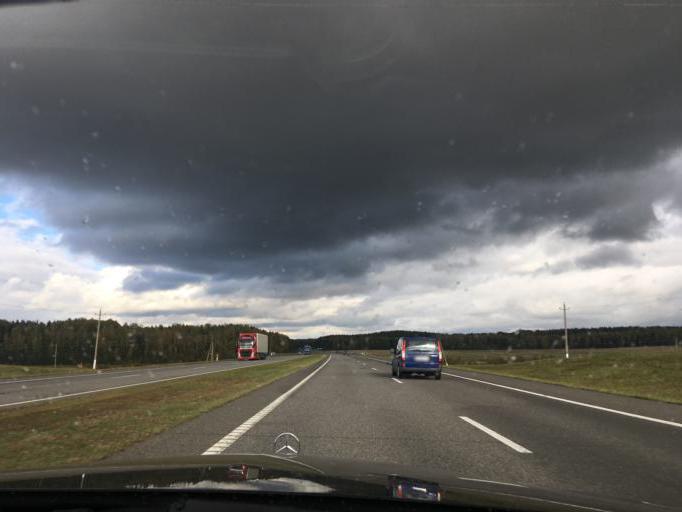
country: BY
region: Vitebsk
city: Talachyn
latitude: 54.4105
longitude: 29.5004
